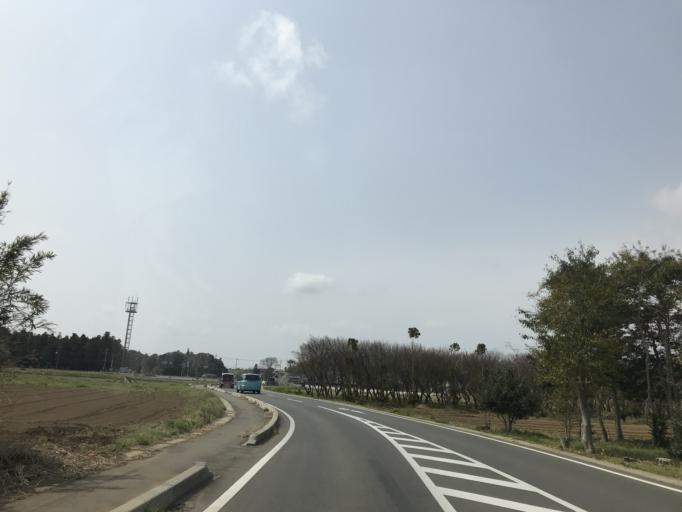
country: JP
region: Ibaraki
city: Naka
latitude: 36.0594
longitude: 140.0898
